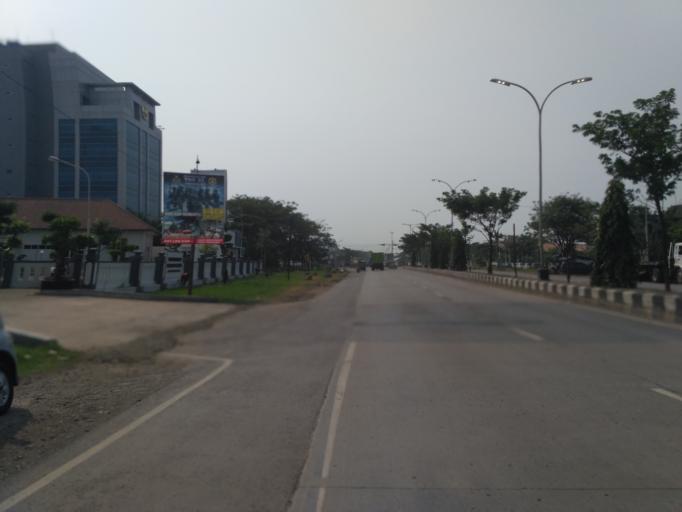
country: ID
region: Central Java
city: Semarang
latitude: -6.9638
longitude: 110.3940
